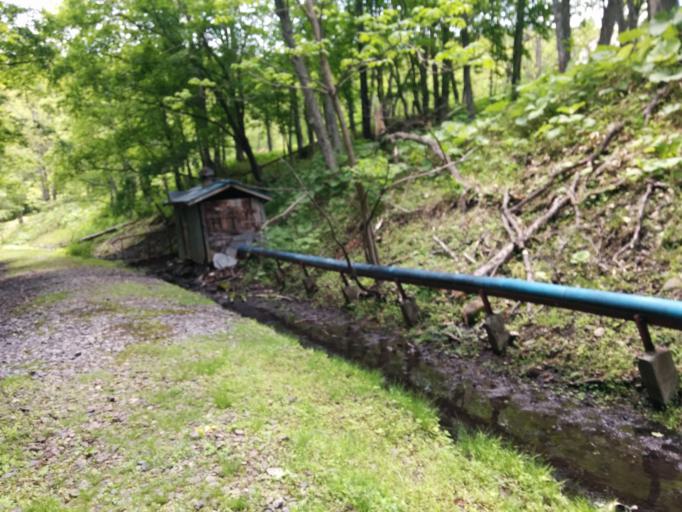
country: JP
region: Hokkaido
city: Otofuke
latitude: 43.3661
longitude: 143.1939
